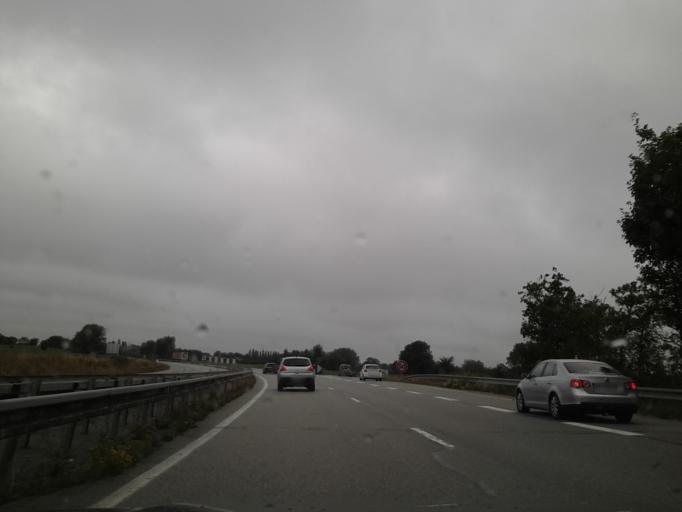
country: FR
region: Lower Normandy
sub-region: Departement de la Manche
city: Sainte-Mere-Eglise
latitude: 49.4007
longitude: -1.3086
